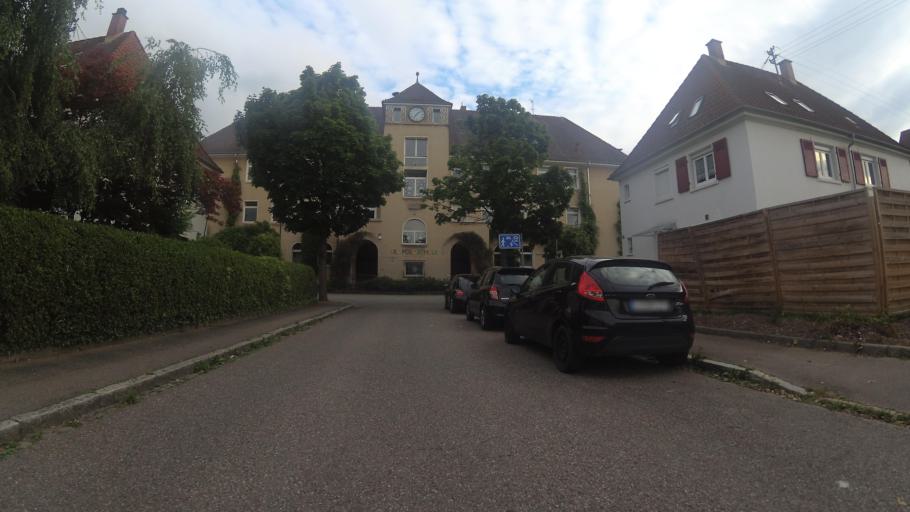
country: DE
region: Baden-Wuerttemberg
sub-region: Freiburg Region
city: Weil am Rhein
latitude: 47.5912
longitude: 7.6191
